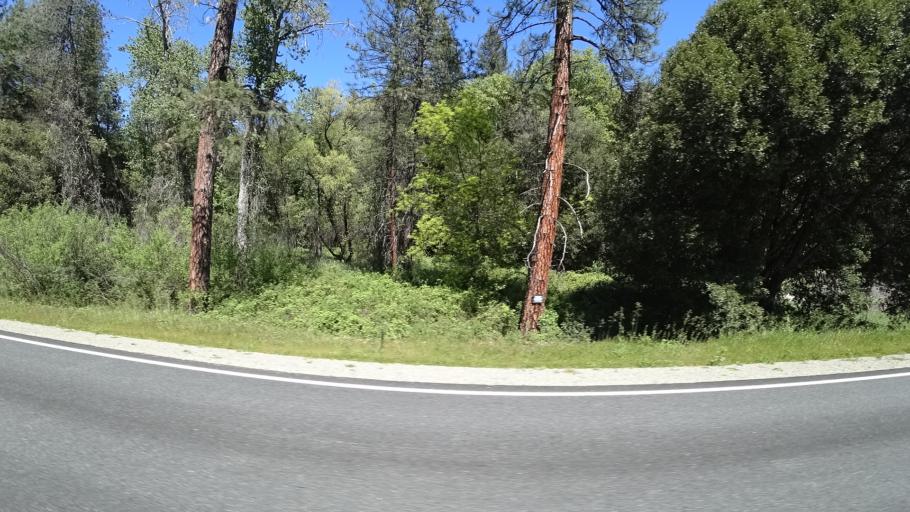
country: US
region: California
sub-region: Trinity County
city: Weaverville
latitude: 40.7413
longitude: -123.0630
